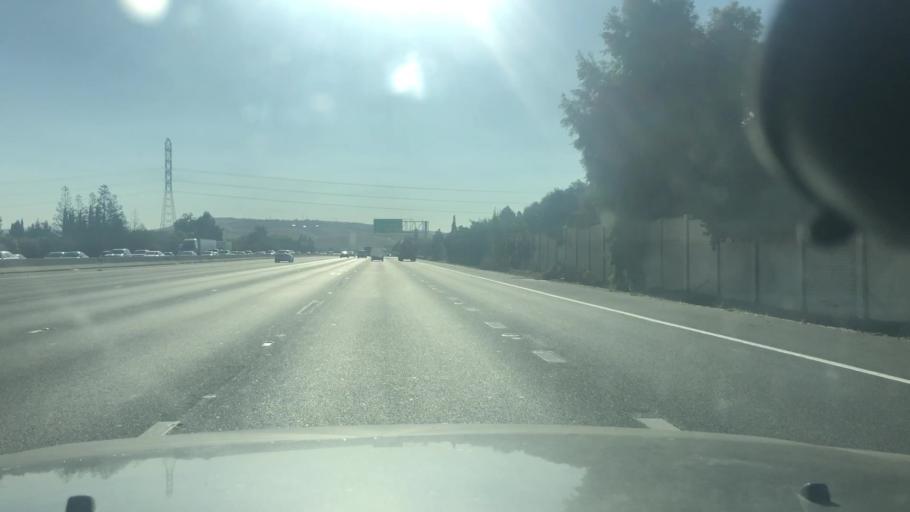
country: US
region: California
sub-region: Santa Clara County
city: Seven Trees
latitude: 37.3112
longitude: -121.8249
